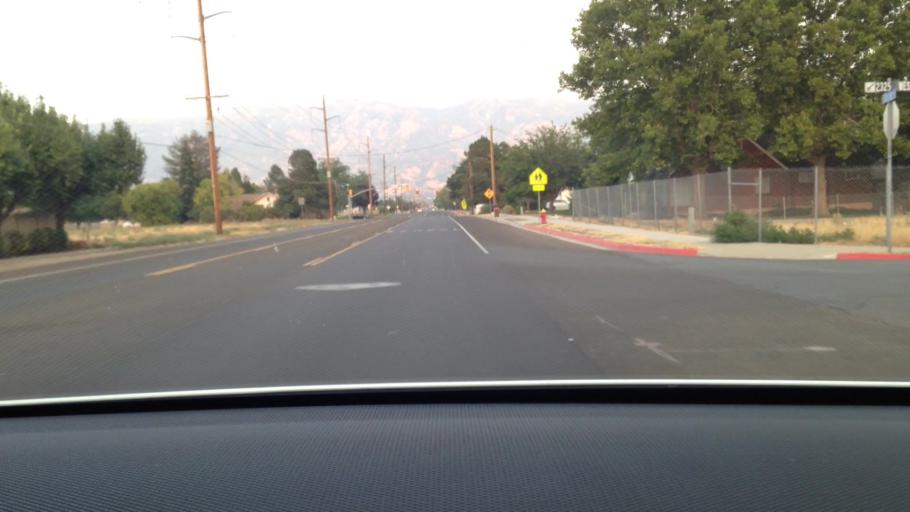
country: US
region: Utah
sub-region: Davis County
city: Clearfield
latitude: 41.0743
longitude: -112.0094
